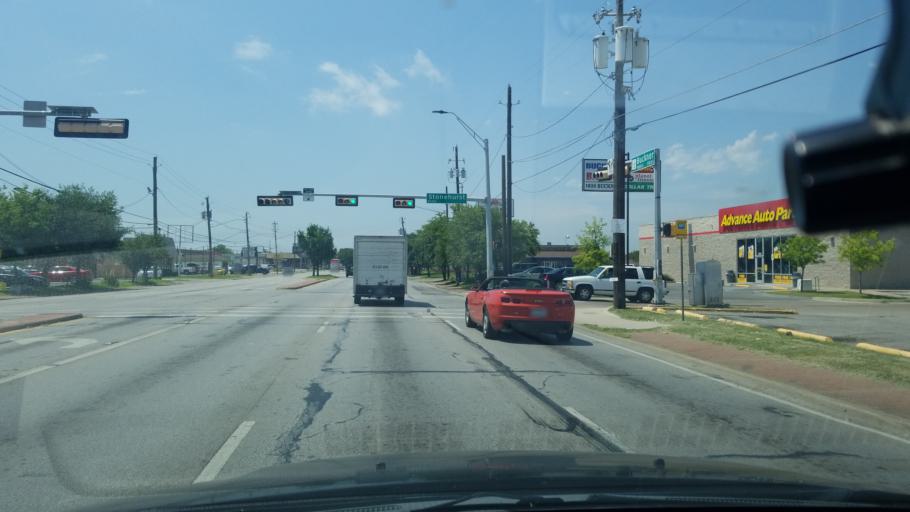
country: US
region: Texas
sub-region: Dallas County
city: Balch Springs
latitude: 32.7418
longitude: -96.6830
